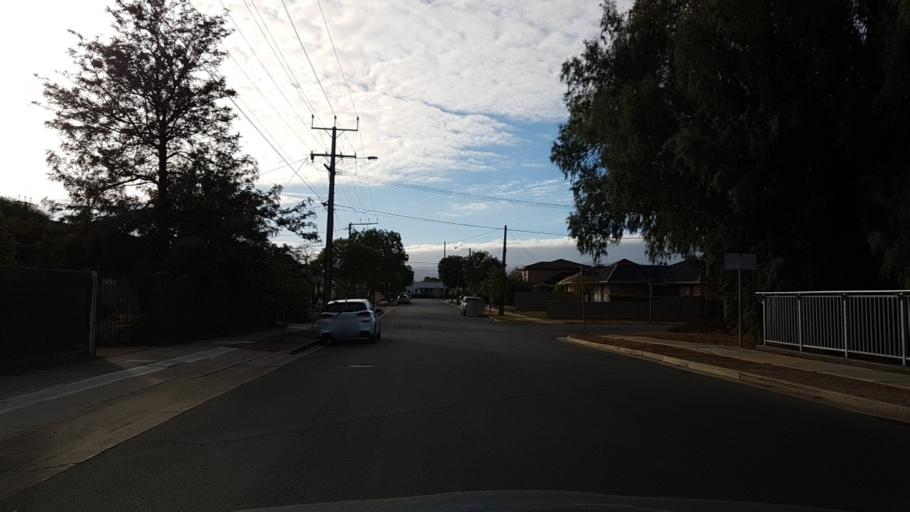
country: AU
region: South Australia
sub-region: City of West Torrens
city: Plympton
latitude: -34.9513
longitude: 138.5517
